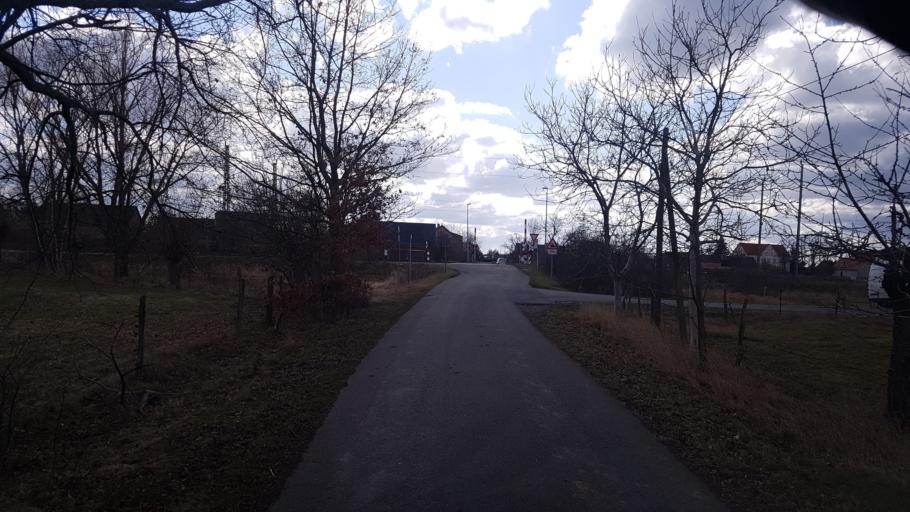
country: DE
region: Brandenburg
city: Falkenberg
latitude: 51.5863
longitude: 13.2135
